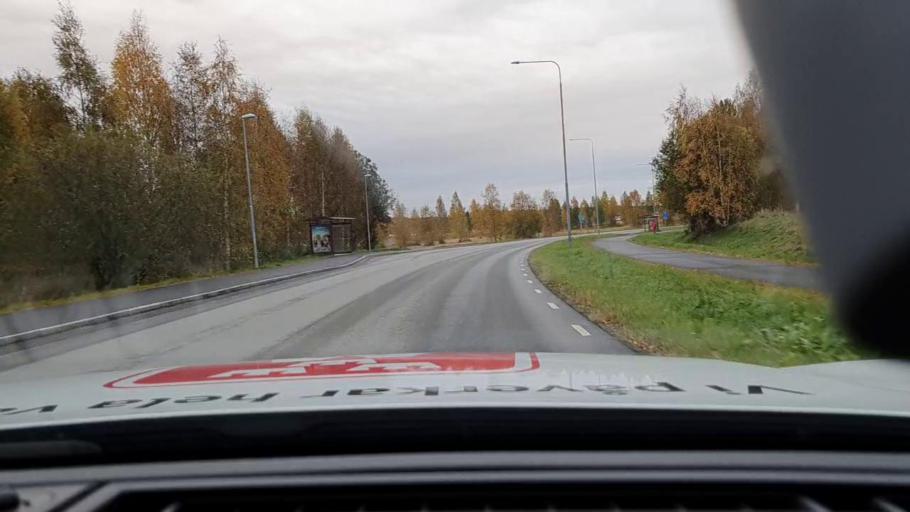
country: SE
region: Norrbotten
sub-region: Bodens Kommun
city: Saevast
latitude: 65.7574
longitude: 21.7539
